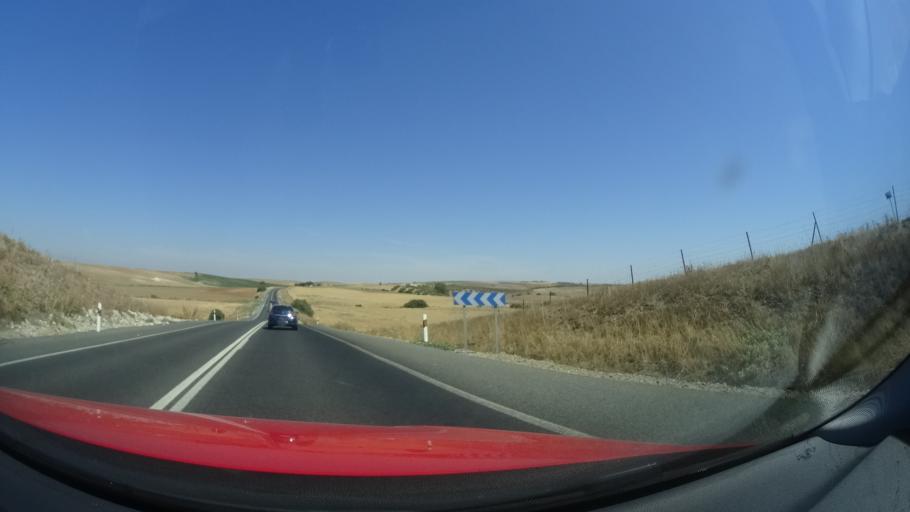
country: ES
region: Andalusia
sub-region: Provincia de Sevilla
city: Las Cabezas de San Juan
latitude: 36.9491
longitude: -5.9020
